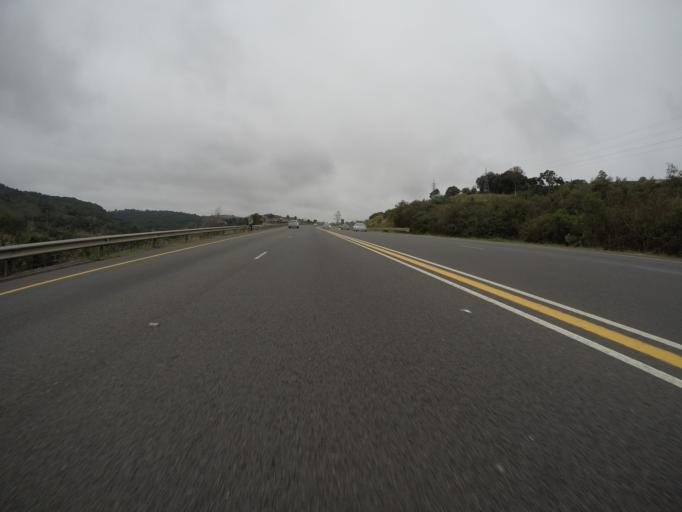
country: ZA
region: Western Cape
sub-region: Eden District Municipality
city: Knysna
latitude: -34.0440
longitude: 23.0873
